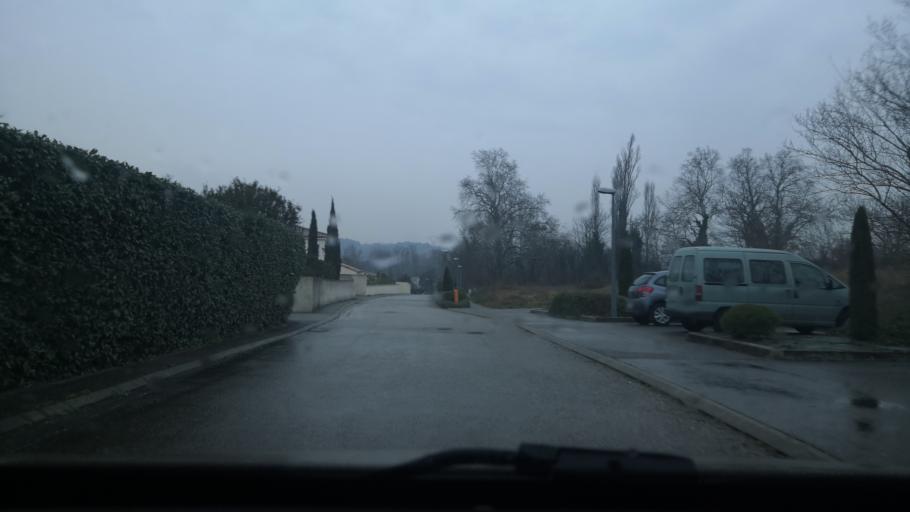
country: FR
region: Rhone-Alpes
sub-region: Departement de la Drome
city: Montboucher-sur-Jabron
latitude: 44.5411
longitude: 4.7990
